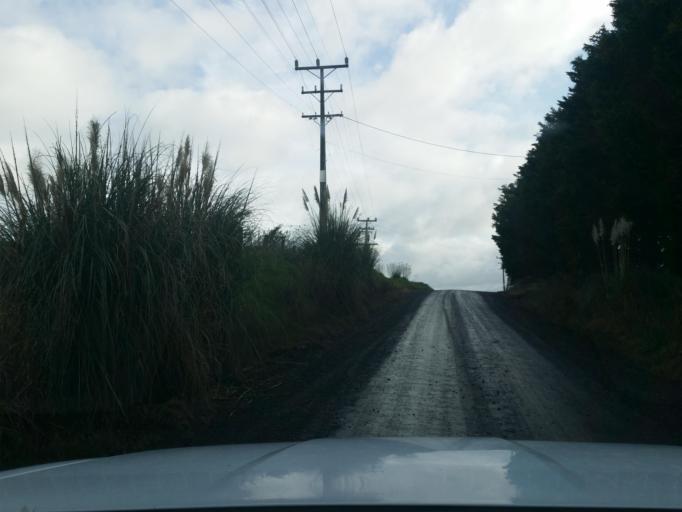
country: NZ
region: Northland
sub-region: Kaipara District
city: Dargaville
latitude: -35.8022
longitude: 173.7380
